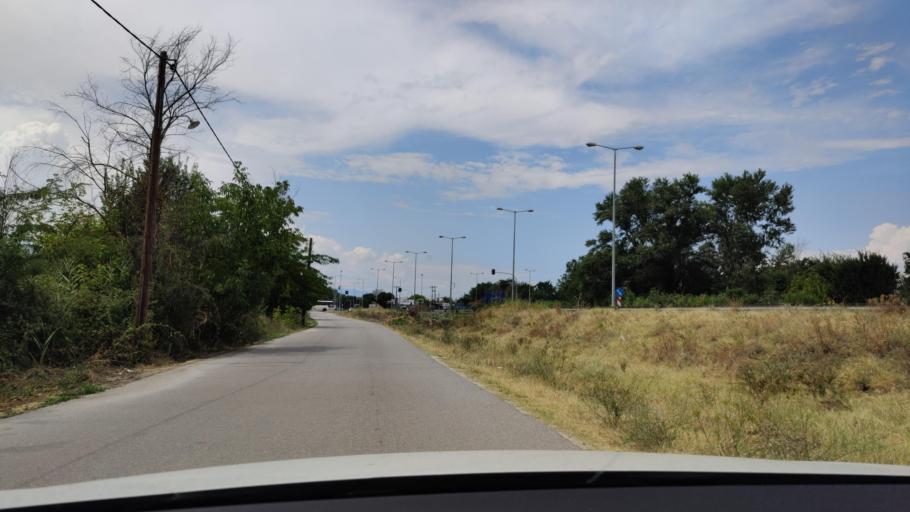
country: GR
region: Central Macedonia
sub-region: Nomos Serron
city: Serres
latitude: 41.0754
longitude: 23.5427
